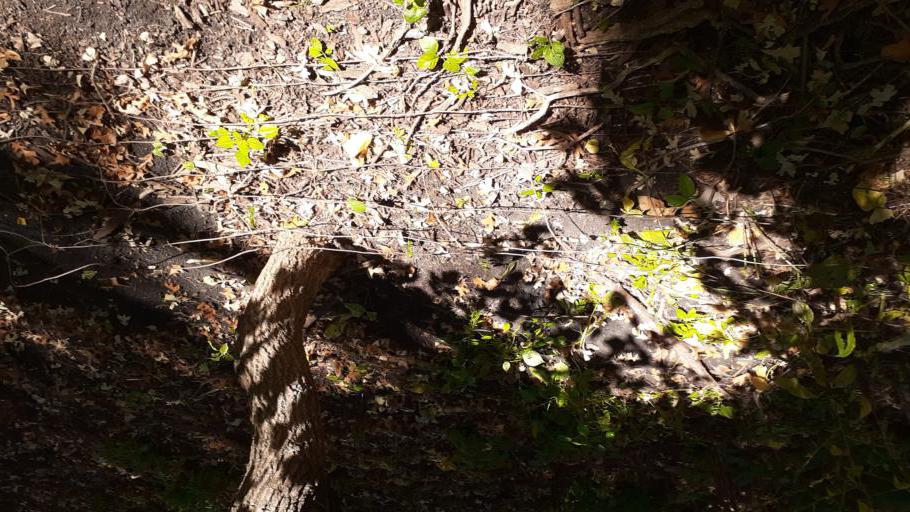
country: US
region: Minnesota
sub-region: Clay County
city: Oakport
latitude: 46.9156
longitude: -96.7648
